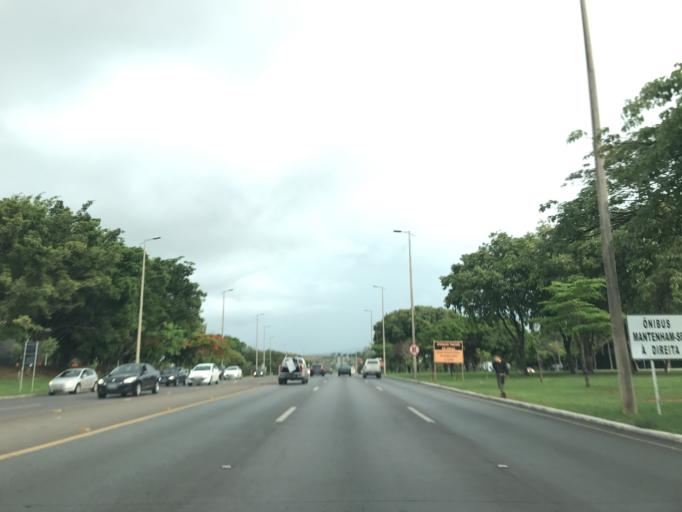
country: BR
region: Federal District
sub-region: Brasilia
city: Brasilia
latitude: -15.7425
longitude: -47.8903
